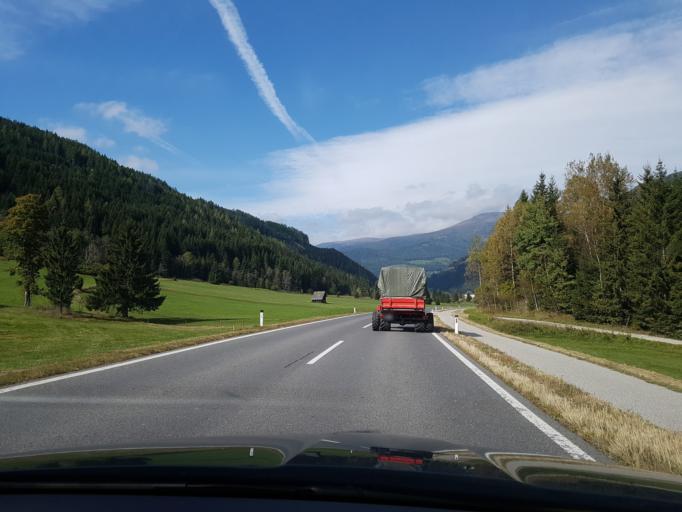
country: AT
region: Carinthia
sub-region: Politischer Bezirk Feldkirchen
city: Gnesau
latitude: 46.7987
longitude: 13.9031
